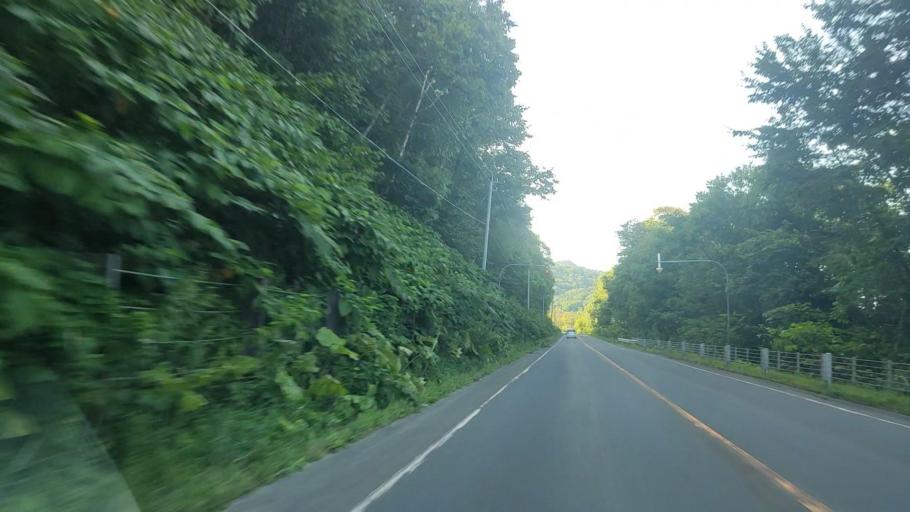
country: JP
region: Hokkaido
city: Nayoro
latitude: 44.7358
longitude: 142.1897
